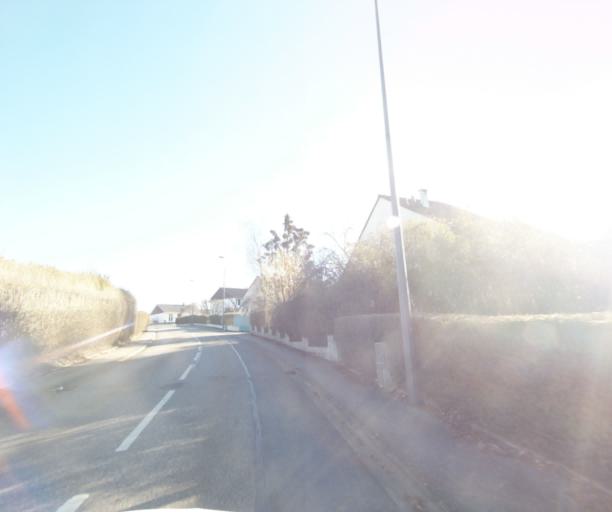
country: FR
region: Lorraine
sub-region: Departement de Meurthe-et-Moselle
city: Vandoeuvre-les-Nancy
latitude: 48.6433
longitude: 6.1952
